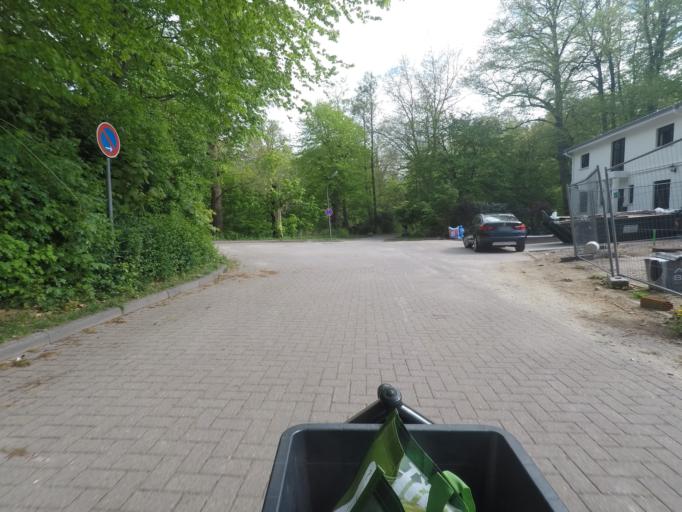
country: DE
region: Hamburg
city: Farmsen-Berne
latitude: 53.6268
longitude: 10.1334
